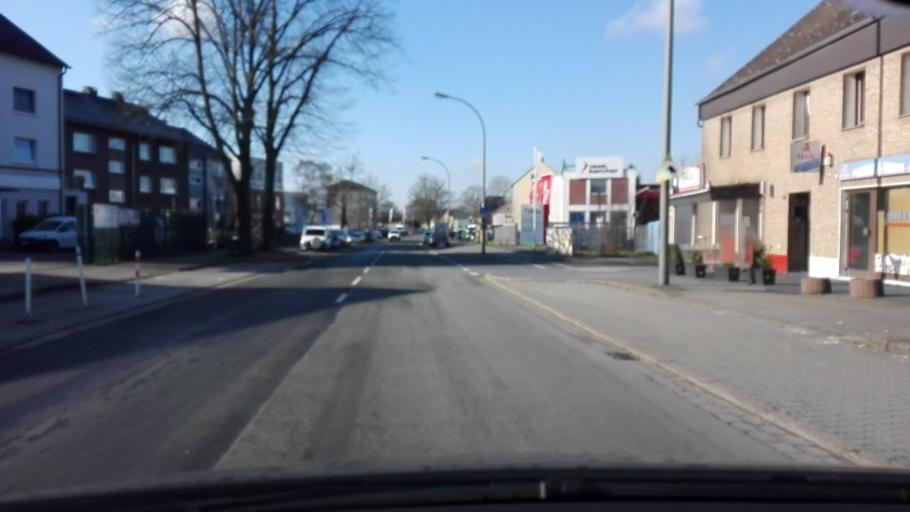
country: DE
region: North Rhine-Westphalia
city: Witten
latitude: 51.4986
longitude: 7.3727
